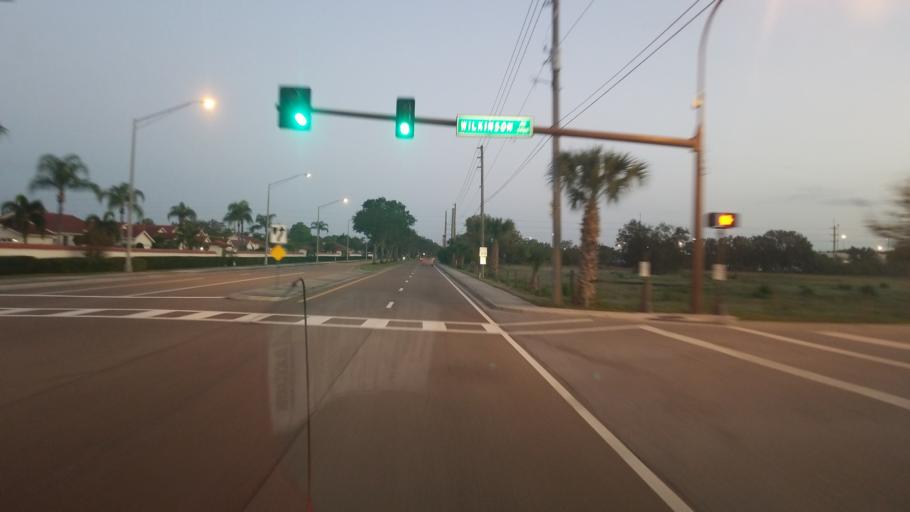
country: US
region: Florida
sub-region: Sarasota County
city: Lake Sarasota
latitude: 27.2888
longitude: -82.4521
